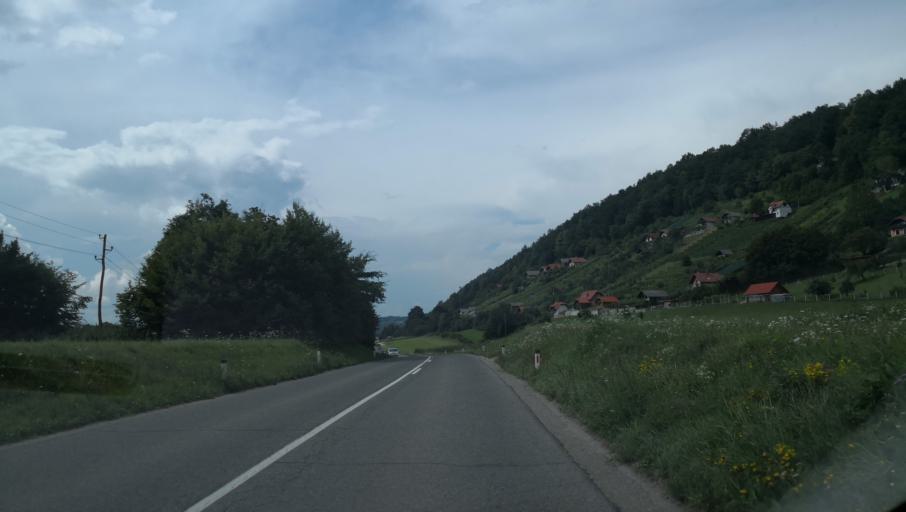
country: SI
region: Zuzemberk
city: Zuzemberk
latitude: 45.8005
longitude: 14.9769
